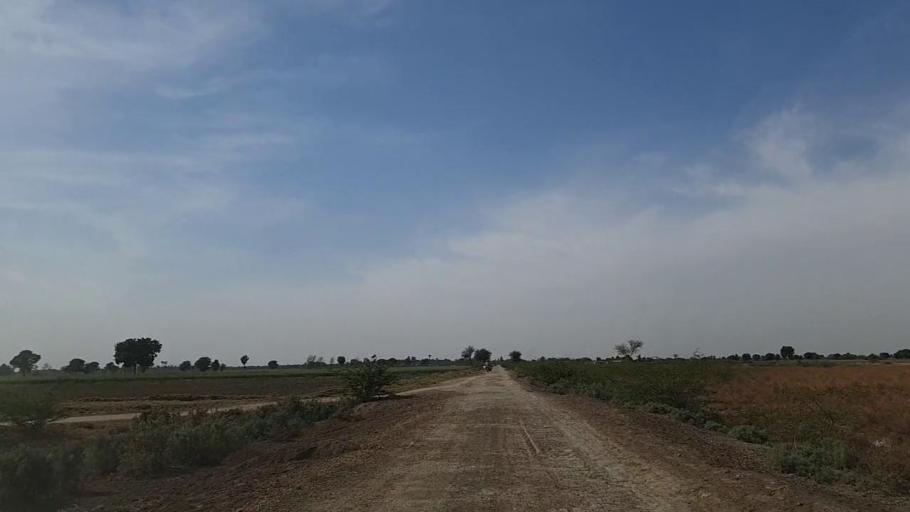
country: PK
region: Sindh
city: Samaro
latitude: 25.2274
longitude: 69.4387
